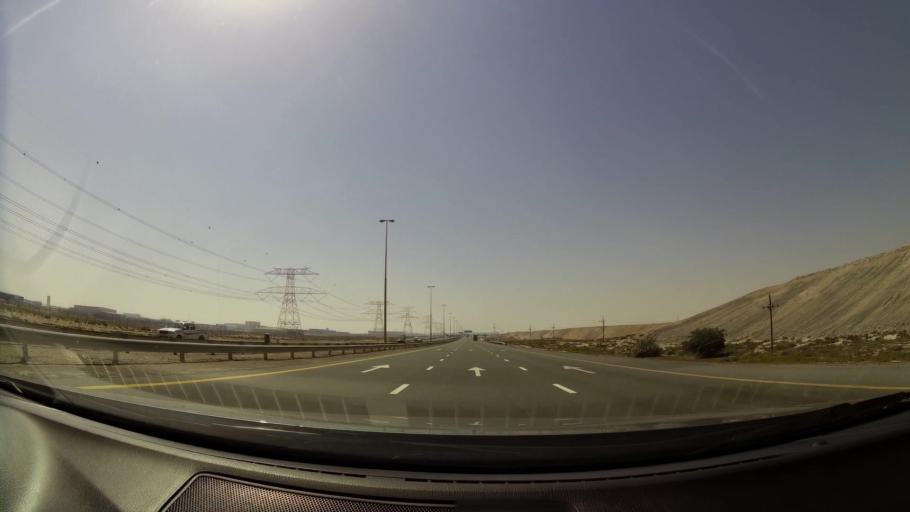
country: AE
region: Dubai
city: Dubai
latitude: 24.9320
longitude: 55.0840
